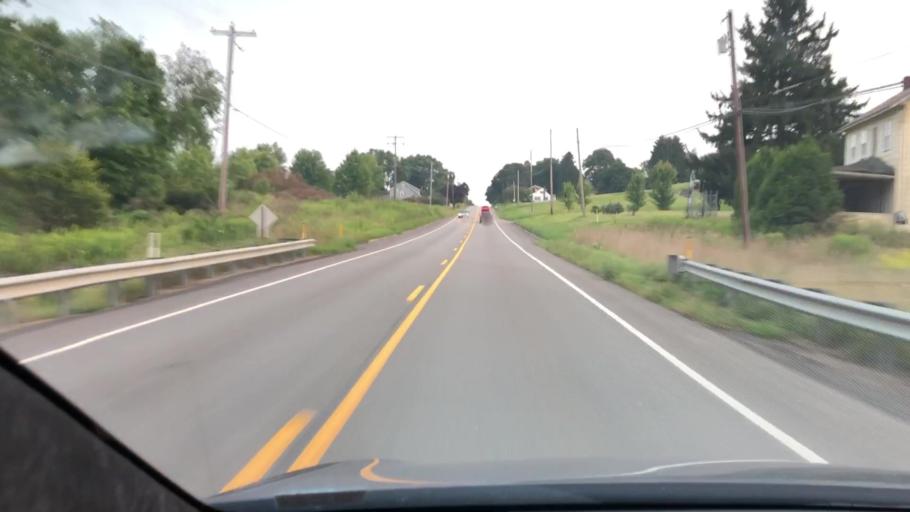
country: US
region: Pennsylvania
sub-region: Butler County
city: Slippery Rock
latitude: 41.1182
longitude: -80.0075
